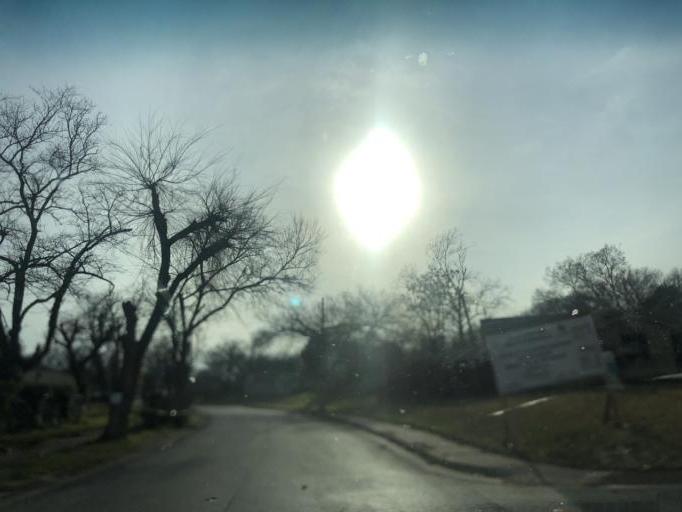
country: US
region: Texas
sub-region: Dallas County
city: Duncanville
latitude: 32.6675
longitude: -96.8977
